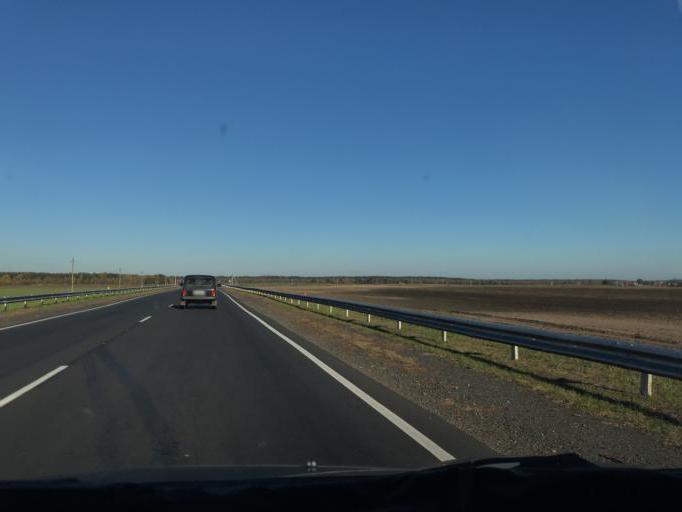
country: BY
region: Gomel
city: Kalinkavichy
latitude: 52.0366
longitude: 29.3452
